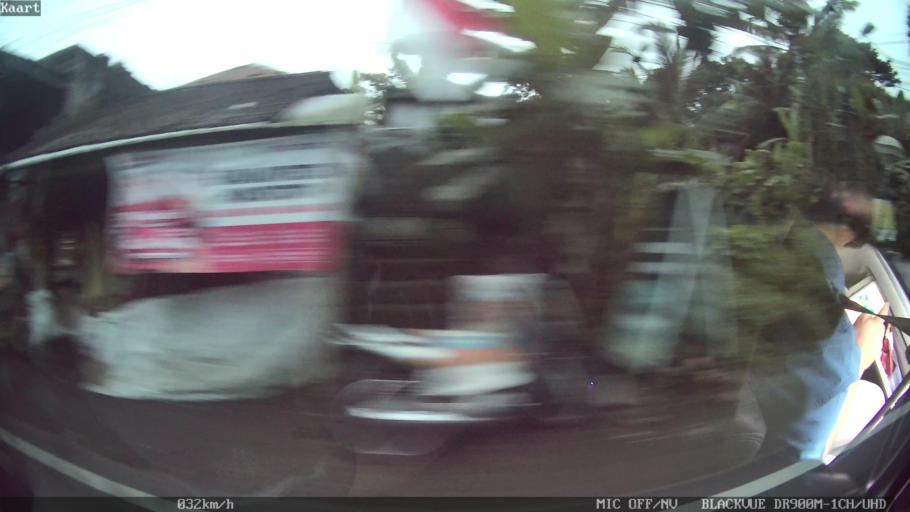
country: ID
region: Bali
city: Badung
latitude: -8.4242
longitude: 115.2461
